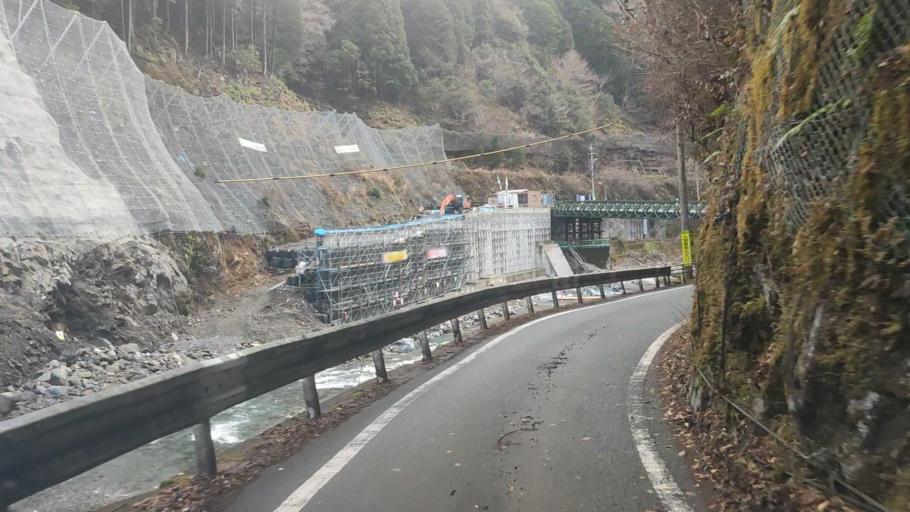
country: JP
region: Kumamoto
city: Matsubase
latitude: 32.4814
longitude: 130.8889
